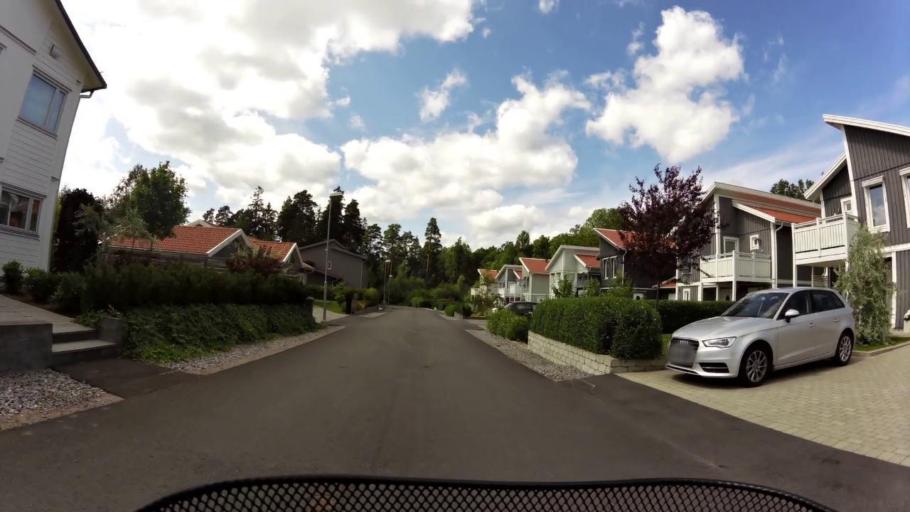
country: SE
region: OEstergoetland
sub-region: Linkopings Kommun
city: Ekangen
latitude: 58.4790
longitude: 15.6349
